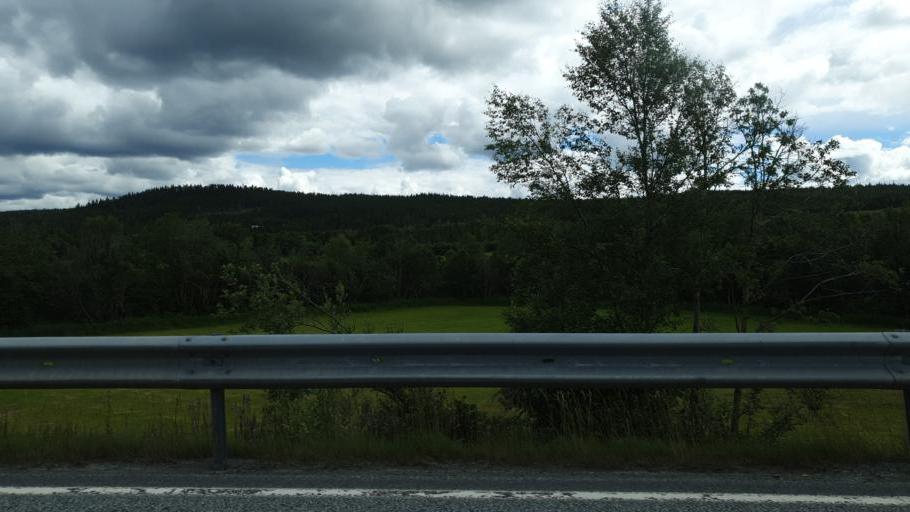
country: NO
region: Sor-Trondelag
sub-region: Rennebu
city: Berkak
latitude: 62.8808
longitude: 10.0918
